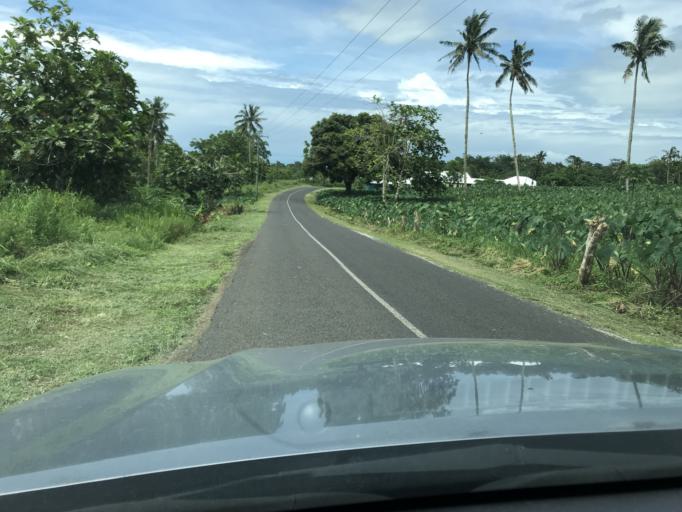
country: WS
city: Fasito`outa
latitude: -13.8665
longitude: -171.9123
